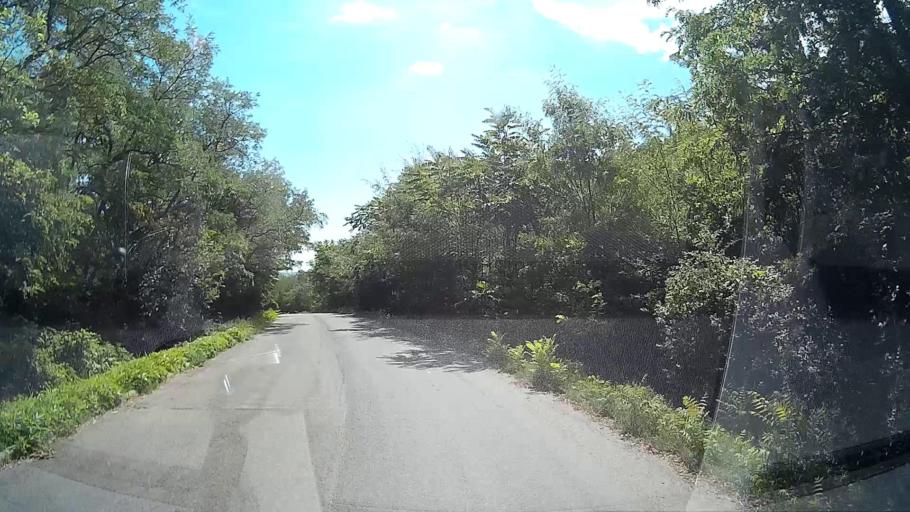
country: HU
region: Pest
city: Leanyfalu
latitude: 47.7046
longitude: 19.0720
